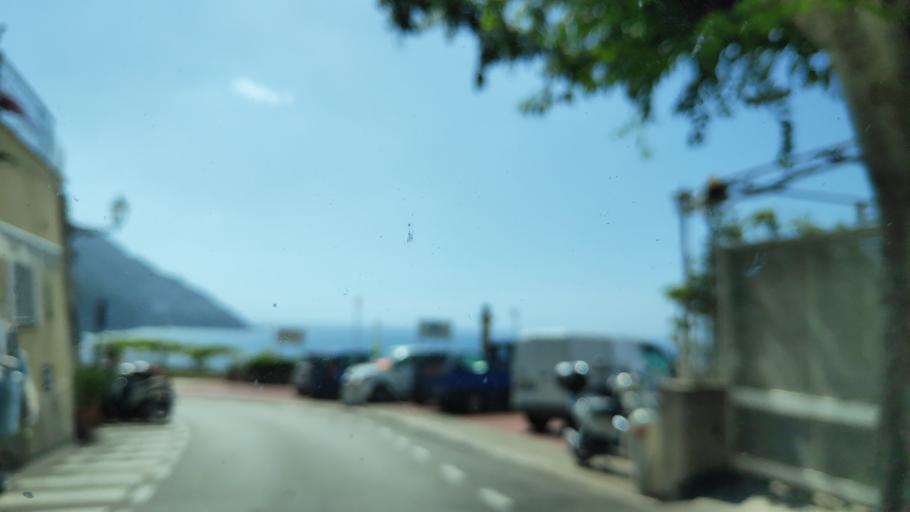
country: IT
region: Campania
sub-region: Provincia di Salerno
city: Positano
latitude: 40.6276
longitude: 14.4839
